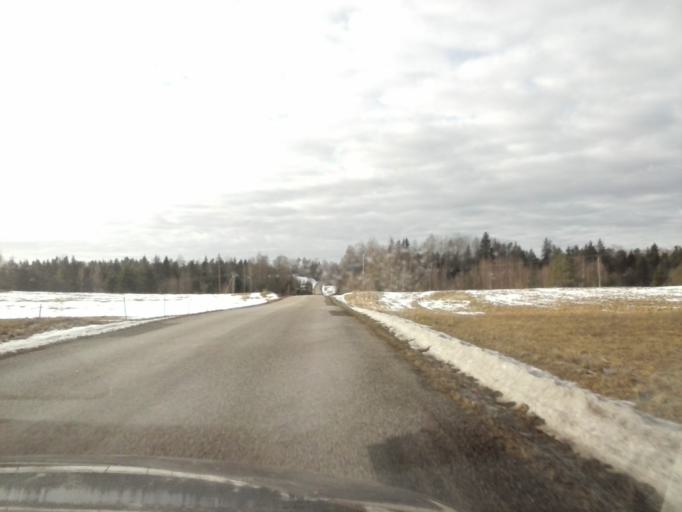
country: EE
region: Tartu
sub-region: Elva linn
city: Elva
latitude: 58.0359
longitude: 26.3530
